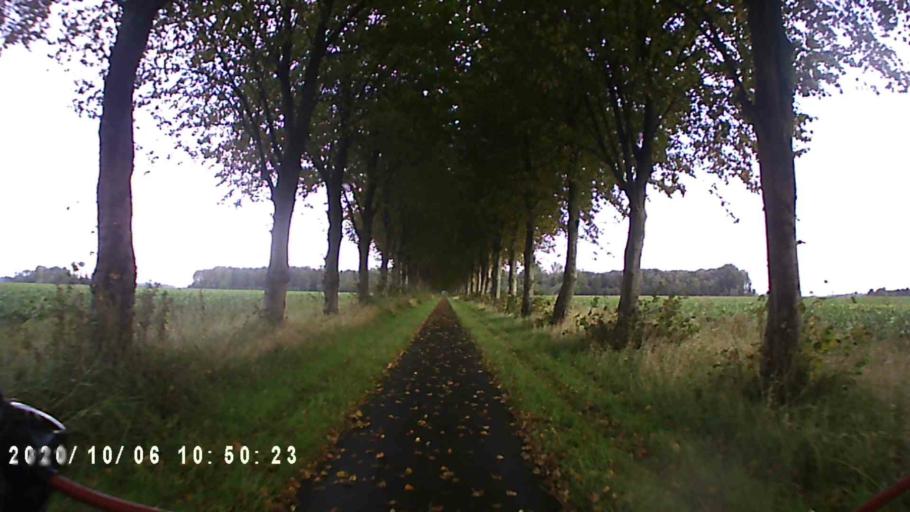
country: NL
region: Groningen
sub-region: Gemeente Zuidhorn
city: Oldehove
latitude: 53.3634
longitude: 6.4102
